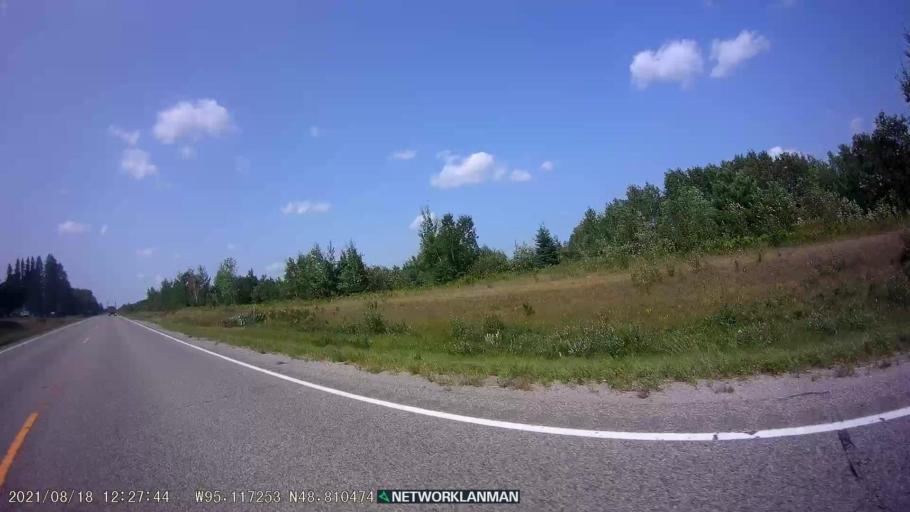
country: US
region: Minnesota
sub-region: Roseau County
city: Warroad
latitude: 48.8106
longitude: -95.1176
